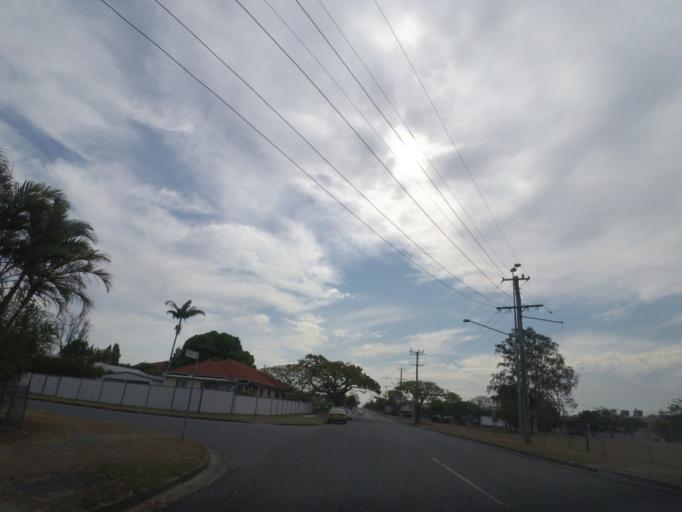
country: AU
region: Queensland
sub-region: Brisbane
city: Richlands
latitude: -27.5918
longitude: 152.9606
